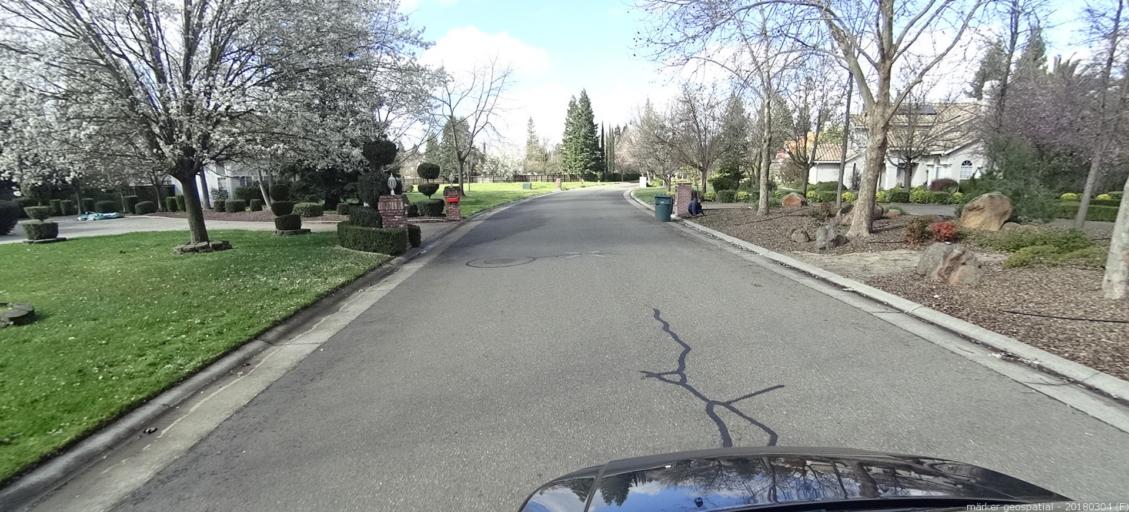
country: US
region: California
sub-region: Sacramento County
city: Vineyard
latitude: 38.4627
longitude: -121.3201
